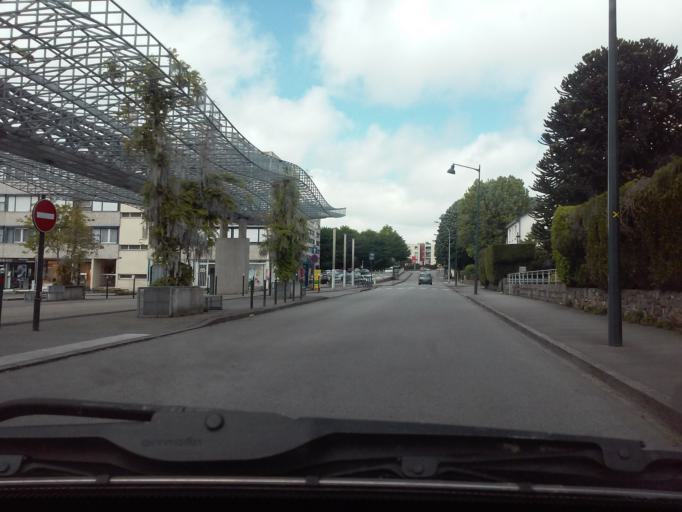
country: FR
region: Brittany
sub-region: Departement d'Ille-et-Vilaine
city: Rennes
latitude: 48.0856
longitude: -1.6921
